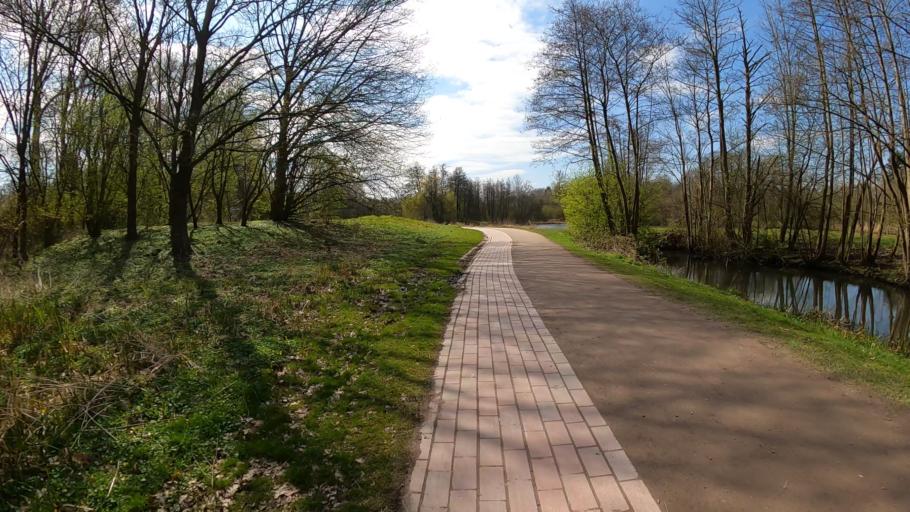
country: DE
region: Hamburg
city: Harburg
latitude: 53.4415
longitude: 9.9790
